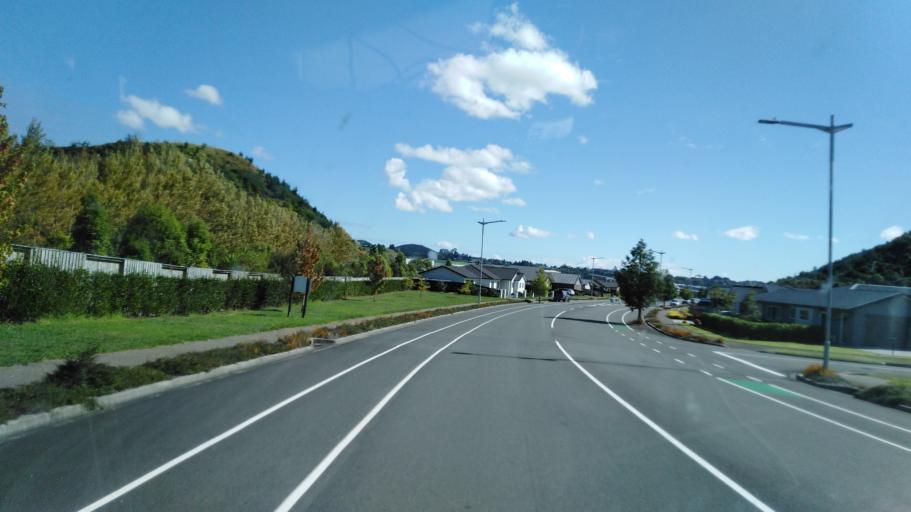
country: NZ
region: Bay of Plenty
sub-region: Tauranga City
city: Tauranga
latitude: -37.7603
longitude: 176.1040
